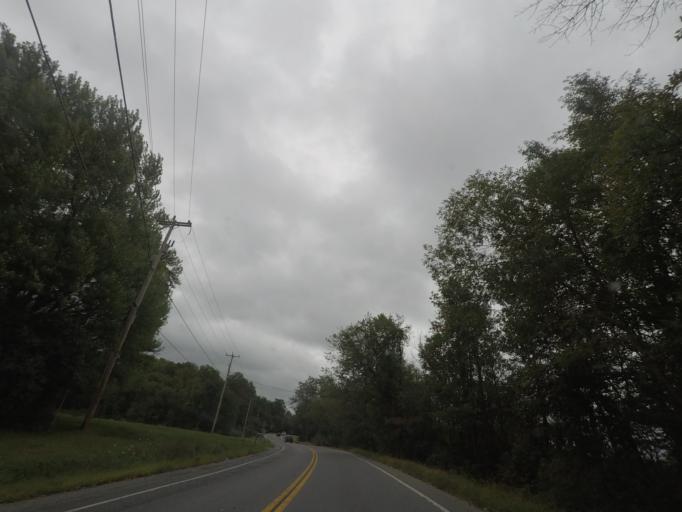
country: US
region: New York
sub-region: Saratoga County
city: Country Knolls
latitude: 42.9313
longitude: -73.7669
